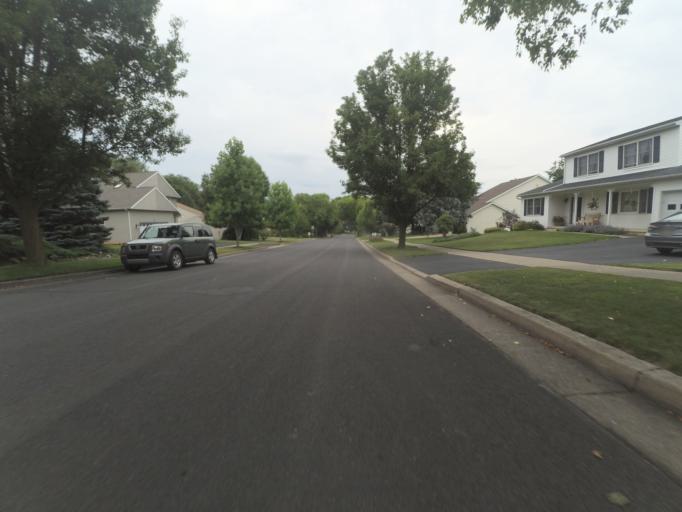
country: US
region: Pennsylvania
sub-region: Centre County
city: State College
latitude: 40.7746
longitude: -77.8683
